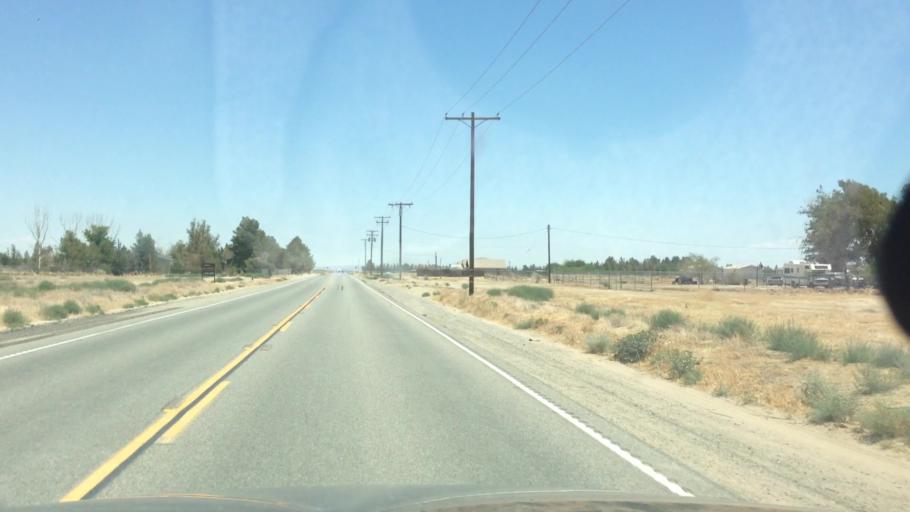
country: US
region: California
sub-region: Los Angeles County
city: Quartz Hill
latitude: 34.7765
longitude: -118.2812
